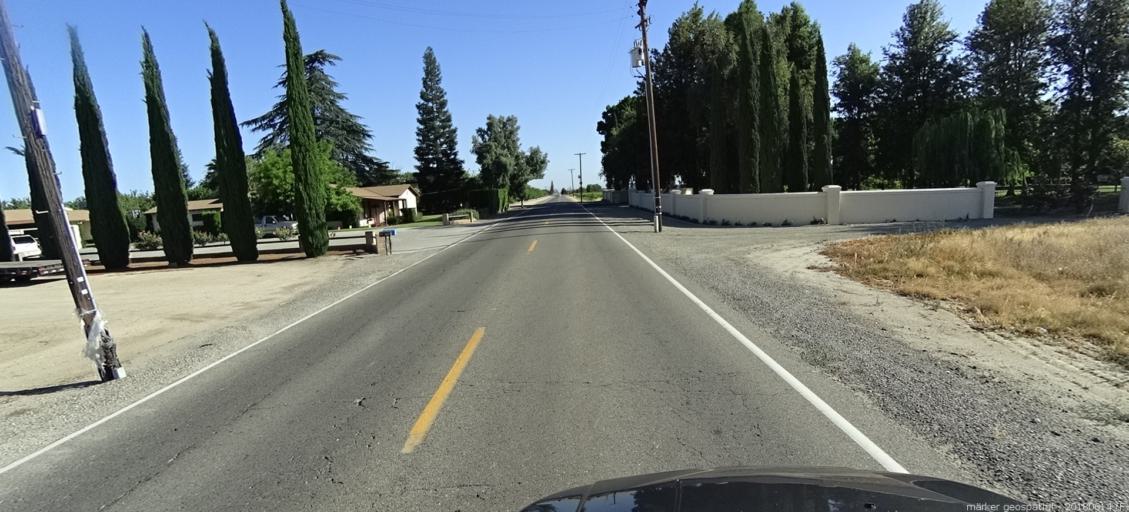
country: US
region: California
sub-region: Madera County
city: Madera
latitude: 36.9481
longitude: -120.1283
